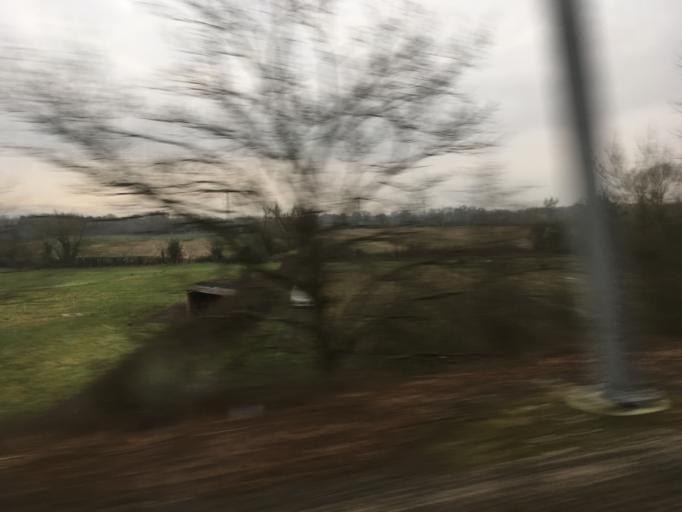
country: GB
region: England
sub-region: Wiltshire
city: Charlton
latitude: 51.5564
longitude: -2.0406
